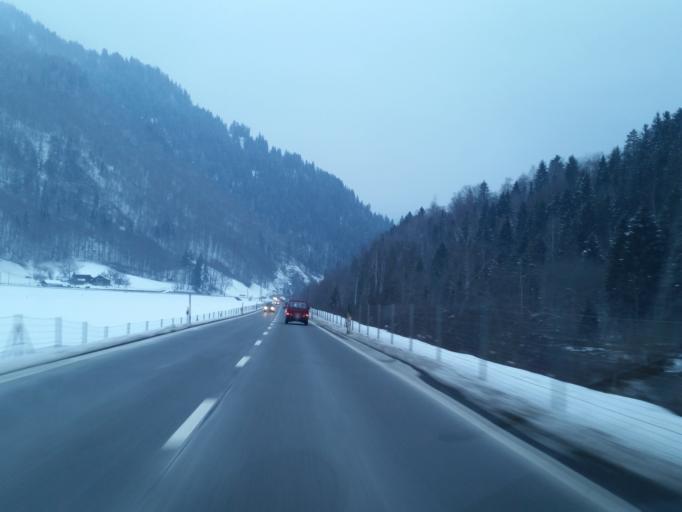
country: CH
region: Grisons
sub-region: Praettigau/Davos District
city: Jenaz
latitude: 46.9423
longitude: 9.7098
